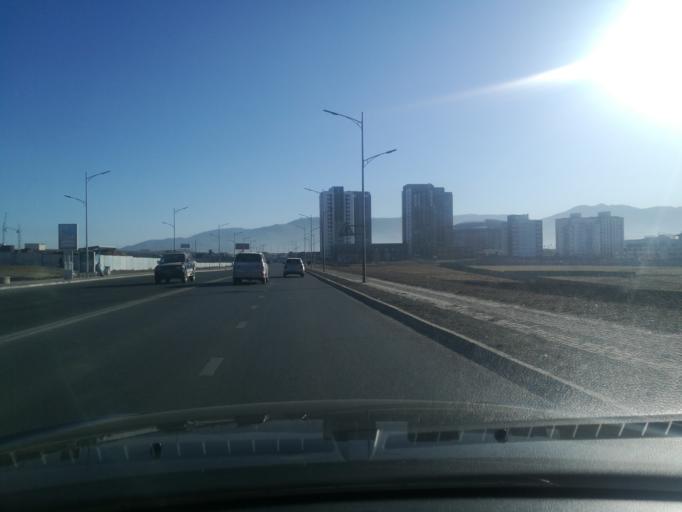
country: MN
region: Ulaanbaatar
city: Ulaanbaatar
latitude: 47.8563
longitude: 106.7761
